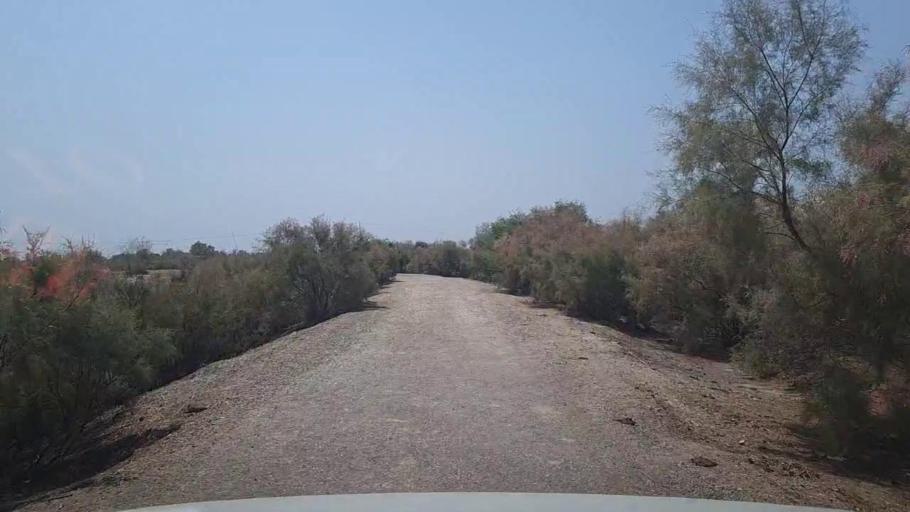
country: PK
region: Sindh
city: Kandhkot
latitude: 28.3103
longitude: 69.3577
